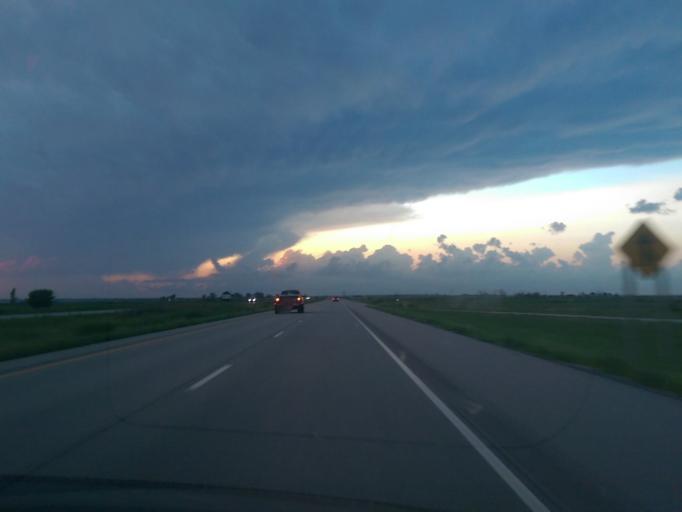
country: US
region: Nebraska
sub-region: Otoe County
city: Nebraska City
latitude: 40.7079
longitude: -95.7963
